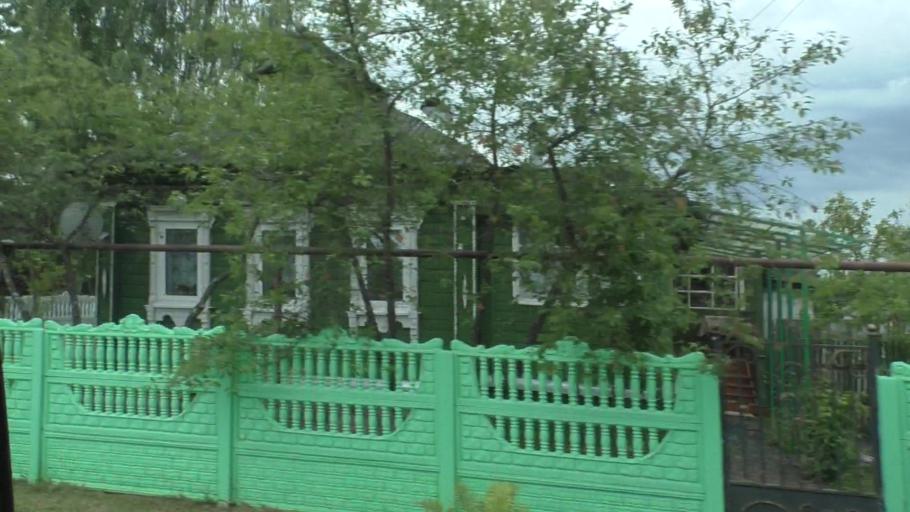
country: RU
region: Moskovskaya
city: Il'inskiy Pogost
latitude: 55.4708
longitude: 38.8957
